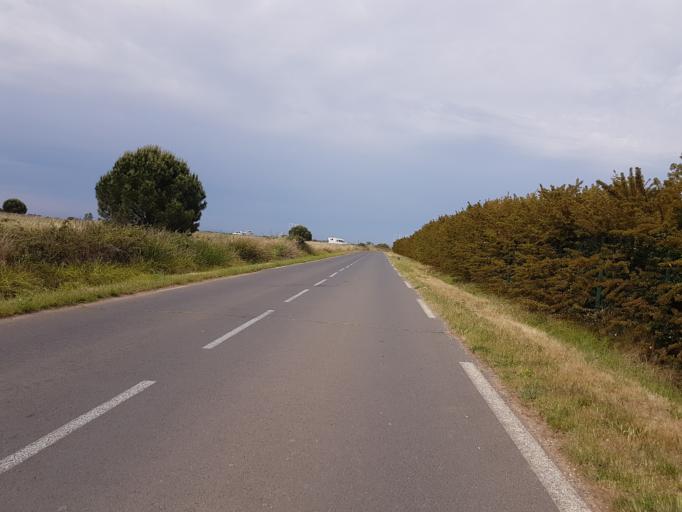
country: FR
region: Languedoc-Roussillon
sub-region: Departement de l'Herault
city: Portiragnes
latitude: 43.3122
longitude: 3.3589
